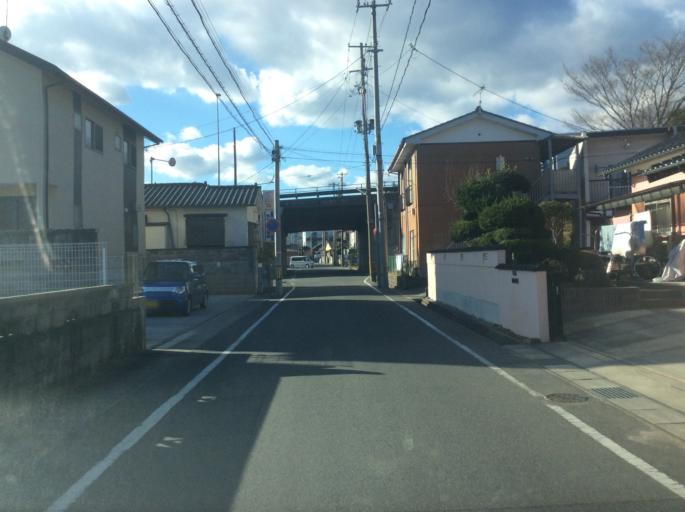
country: JP
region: Fukushima
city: Iwaki
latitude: 37.0560
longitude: 140.9094
